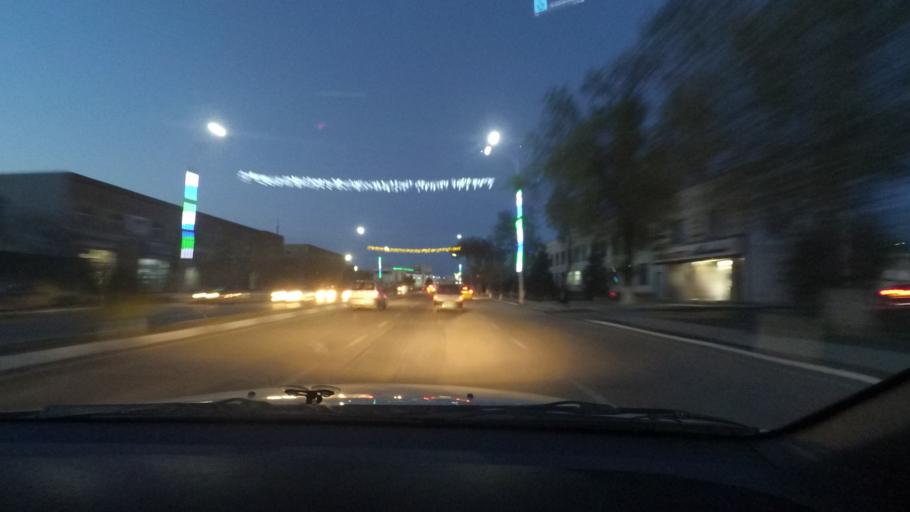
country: UZ
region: Bukhara
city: Bukhara
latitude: 39.7804
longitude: 64.4108
